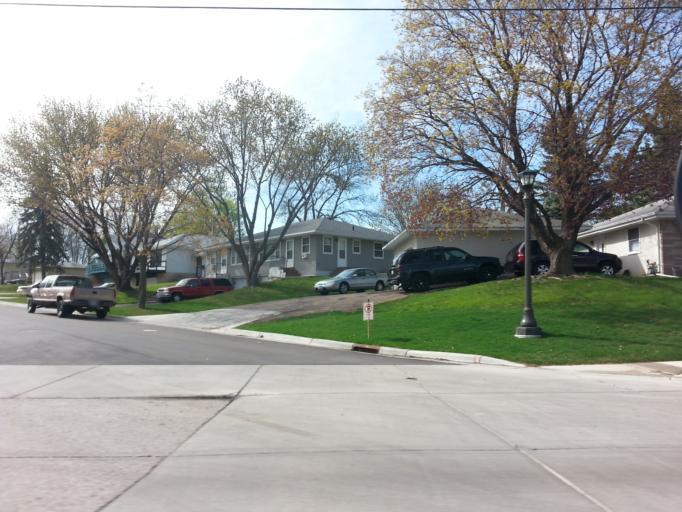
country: US
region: Minnesota
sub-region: Ramsey County
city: Little Canada
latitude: 44.9892
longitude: -93.0721
